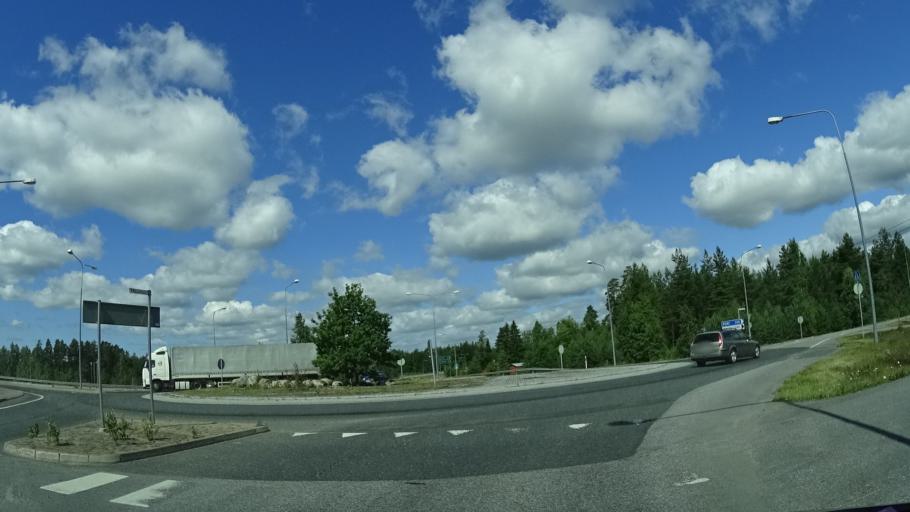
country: FI
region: Varsinais-Suomi
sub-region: Turku
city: Raisio
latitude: 60.5069
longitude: 22.1594
